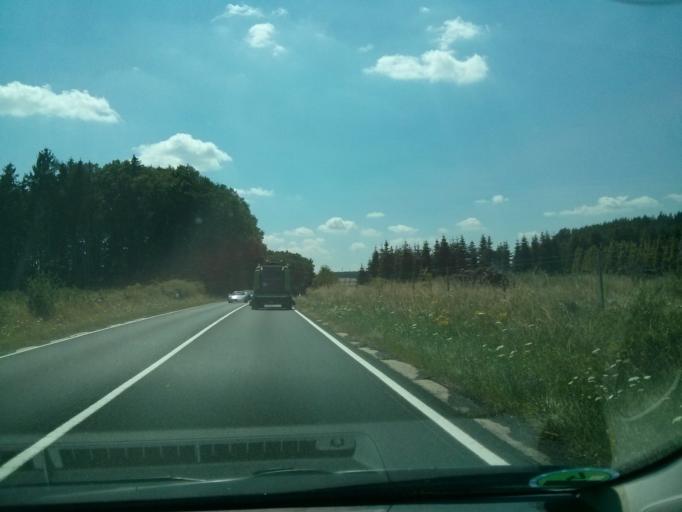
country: DE
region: Rheinland-Pfalz
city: Kalenborn
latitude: 50.5678
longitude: 7.0238
